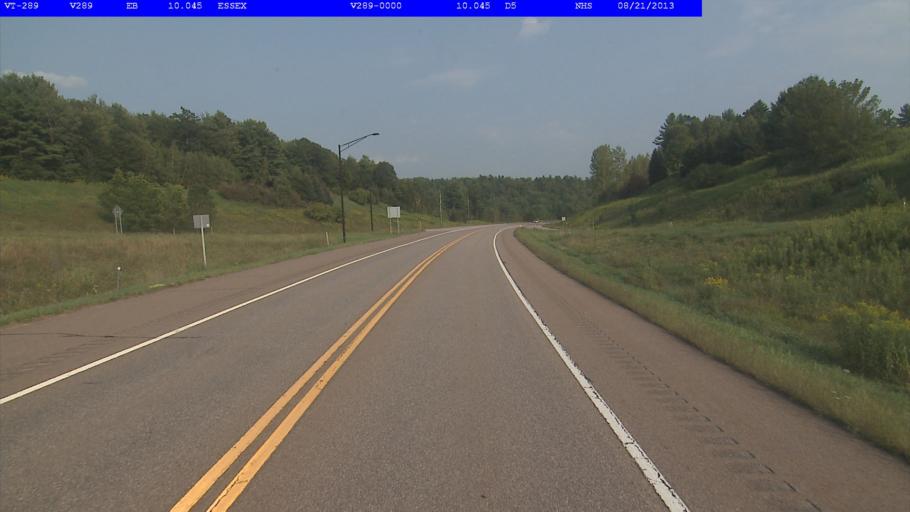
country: US
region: Vermont
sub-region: Chittenden County
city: Essex Junction
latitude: 44.5042
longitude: -73.0774
